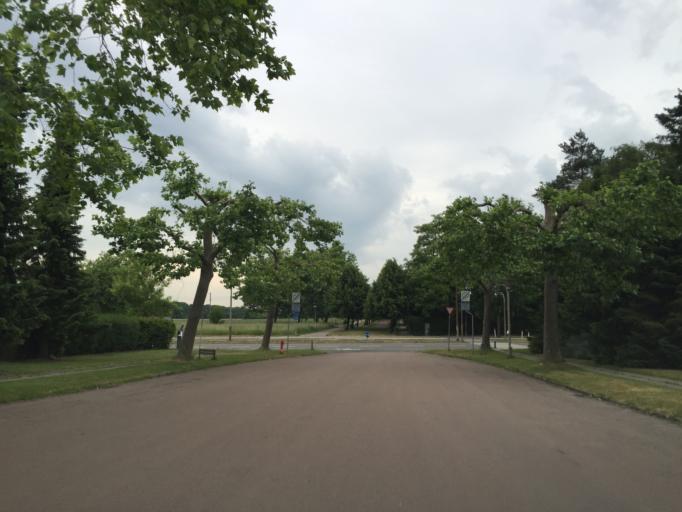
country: DK
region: Capital Region
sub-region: Lyngby-Tarbaek Kommune
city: Kongens Lyngby
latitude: 55.7744
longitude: 12.5293
